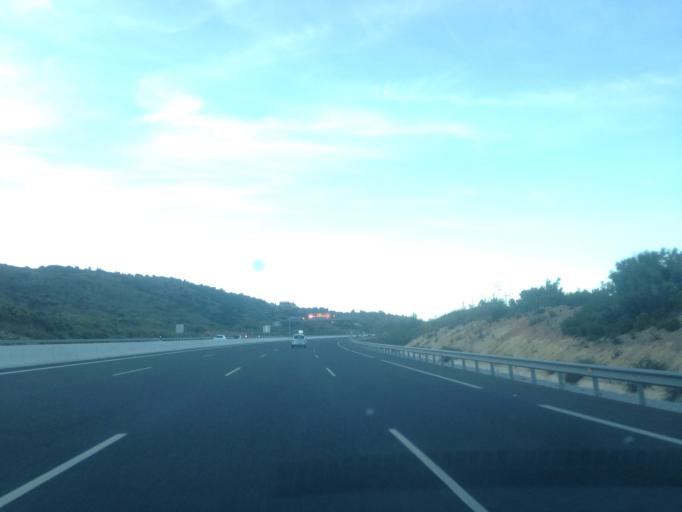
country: ES
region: Andalusia
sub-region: Provincia de Malaga
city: Torremolinos
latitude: 36.6371
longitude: -4.5140
